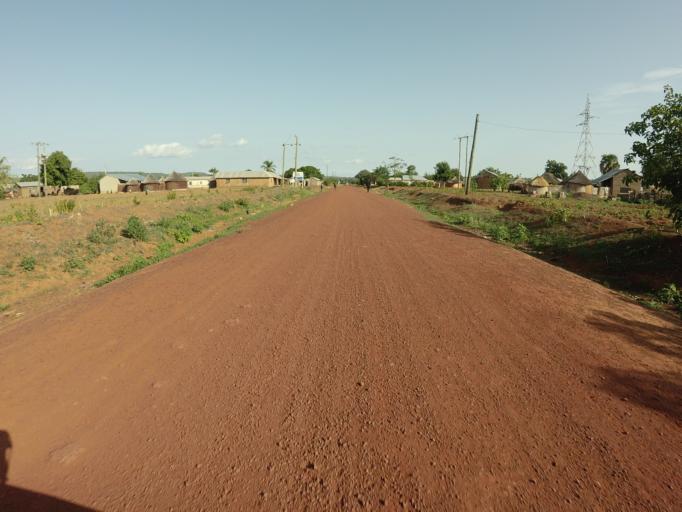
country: GH
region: Upper East
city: Bawku
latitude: 10.6276
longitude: -0.1797
